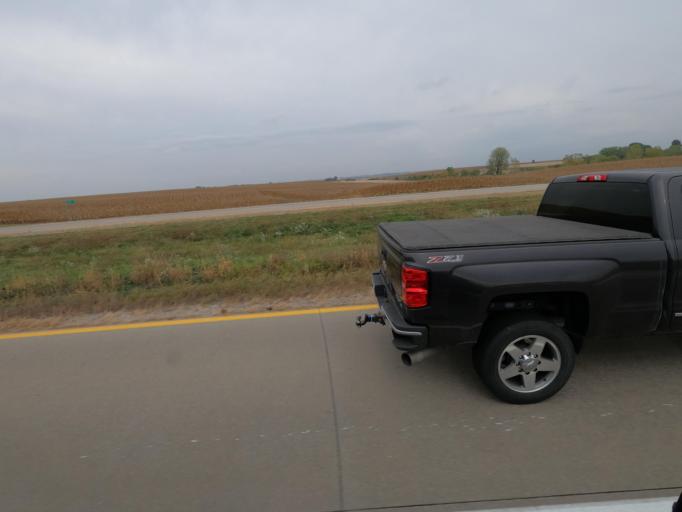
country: US
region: Iowa
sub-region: Marion County
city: Pella
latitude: 41.3625
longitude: -92.7825
